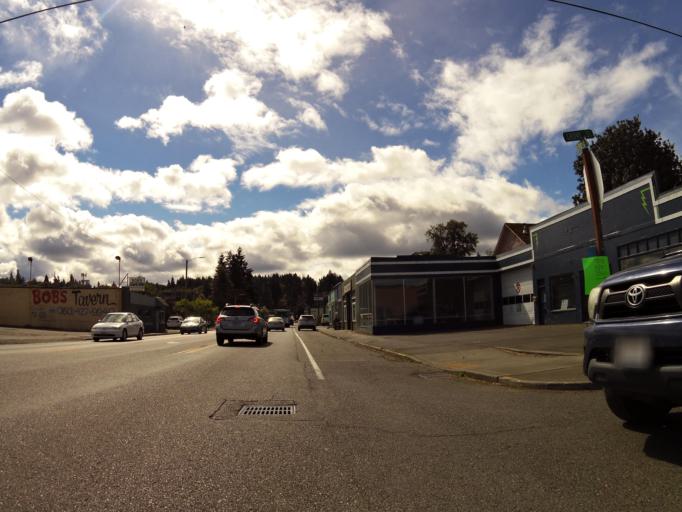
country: US
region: Washington
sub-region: Mason County
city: Shelton
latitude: 47.2112
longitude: -123.1004
